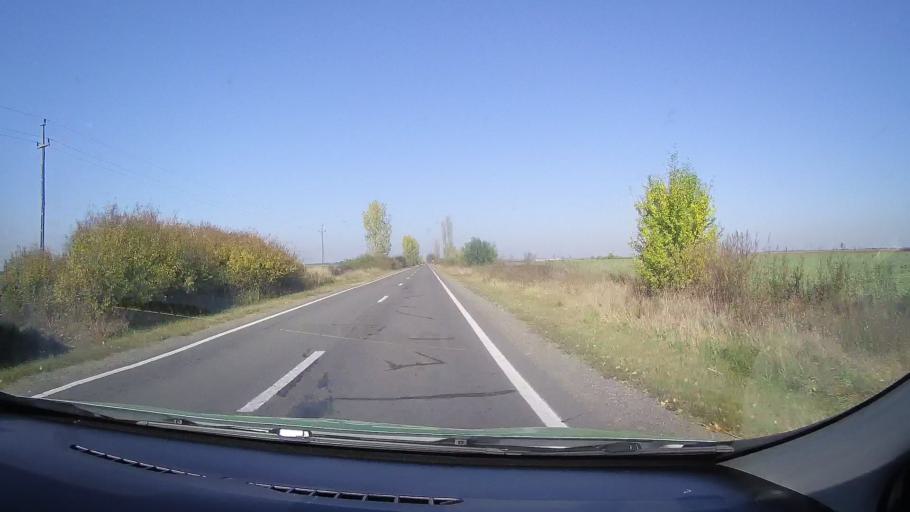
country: RO
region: Satu Mare
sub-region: Comuna Urziceni
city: Urziceni
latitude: 47.7096
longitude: 22.4286
